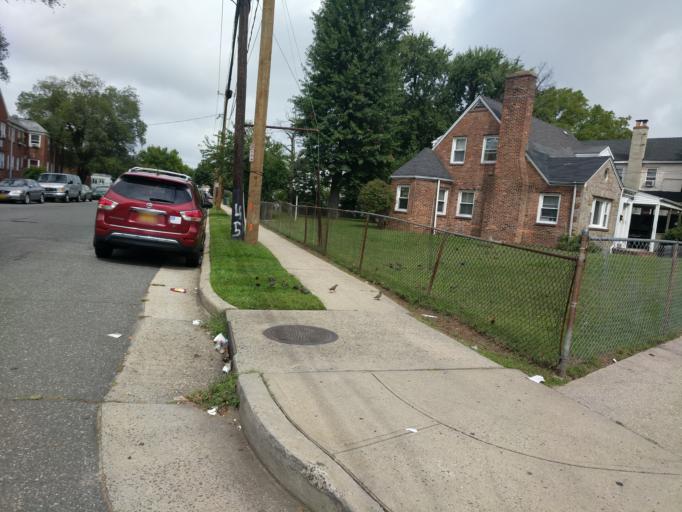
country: US
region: New York
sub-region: Nassau County
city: Hempstead
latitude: 40.7110
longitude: -73.6160
